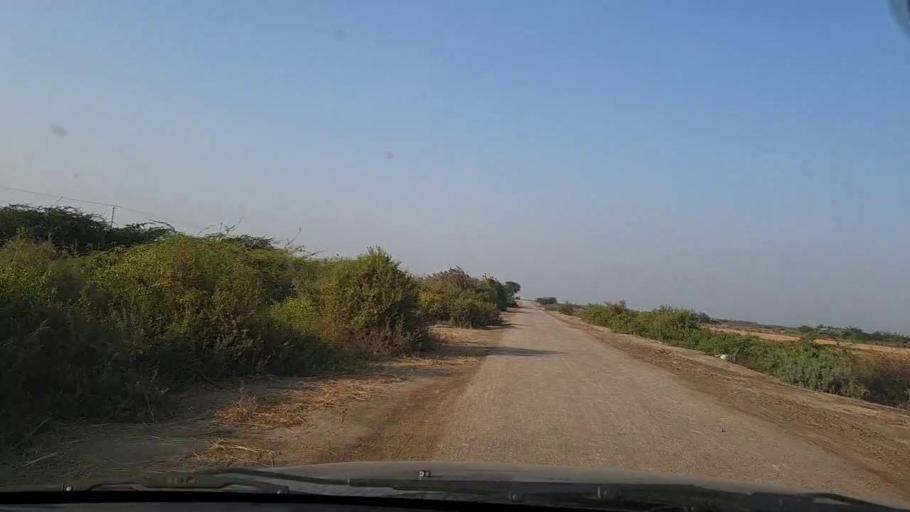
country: PK
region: Sindh
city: Chuhar Jamali
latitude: 24.3044
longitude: 67.7555
